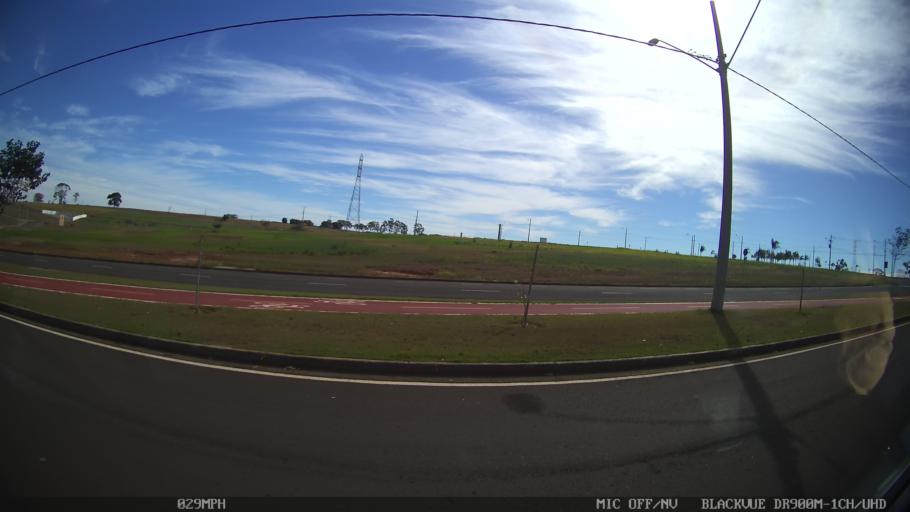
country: BR
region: Sao Paulo
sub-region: Sao Jose Do Rio Preto
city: Sao Jose do Rio Preto
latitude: -20.8549
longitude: -49.3759
